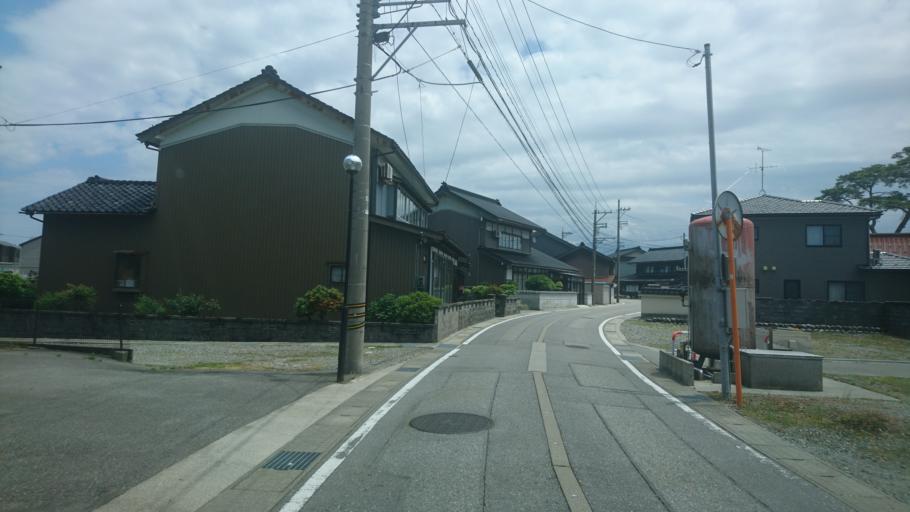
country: JP
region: Toyama
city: Nyuzen
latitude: 36.9335
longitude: 137.4955
